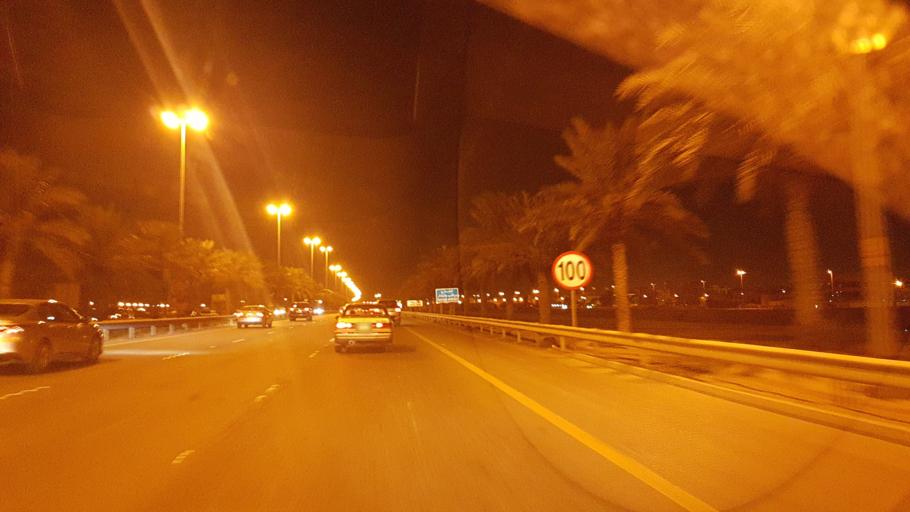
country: BH
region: Muharraq
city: Al Hadd
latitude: 26.2521
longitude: 50.6594
